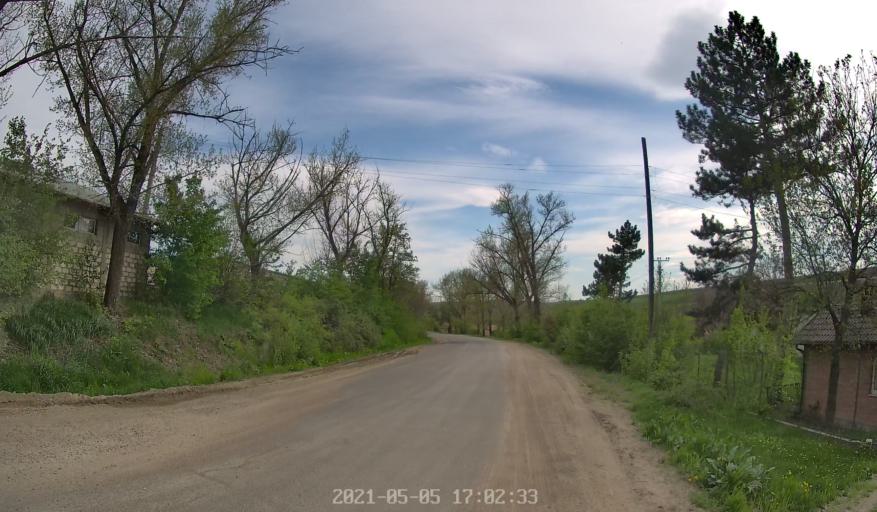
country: MD
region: Chisinau
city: Vadul lui Voda
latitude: 47.0584
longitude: 29.1322
